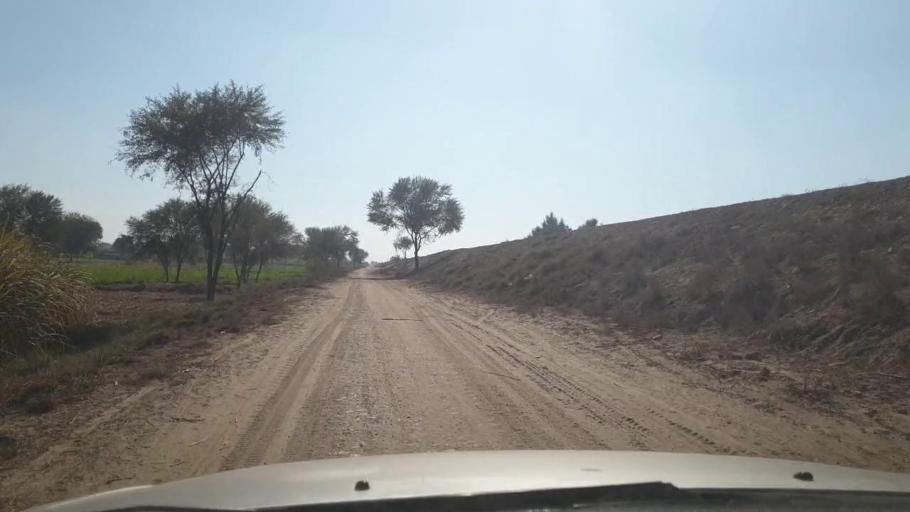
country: PK
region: Sindh
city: Ghotki
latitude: 28.0287
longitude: 69.2105
